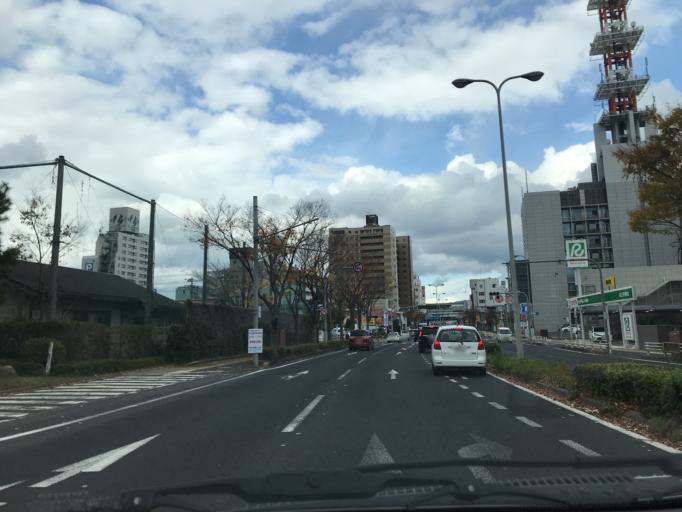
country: JP
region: Shimane
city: Matsue-shi
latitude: 35.4613
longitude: 133.0655
